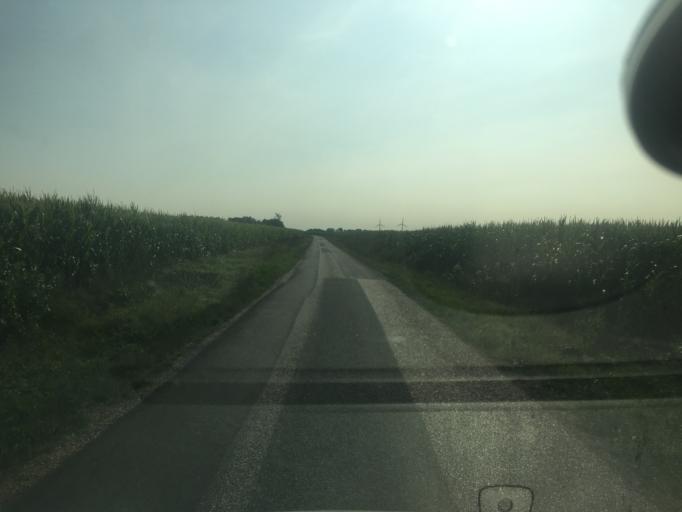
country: DK
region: South Denmark
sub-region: Tonder Kommune
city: Tonder
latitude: 54.9945
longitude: 8.9133
